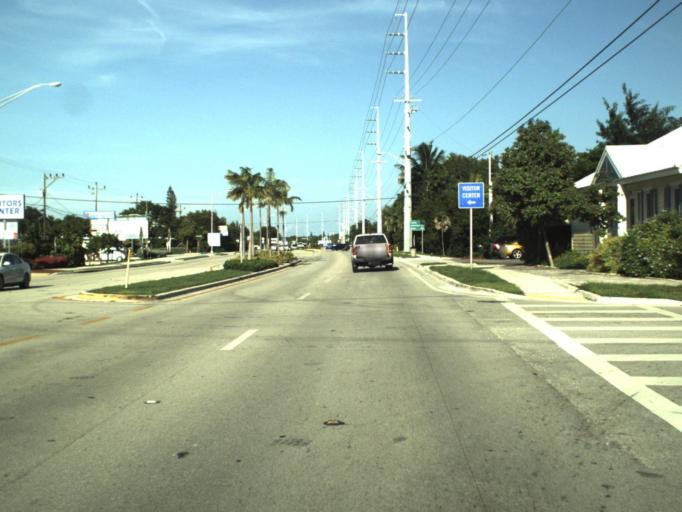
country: US
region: Florida
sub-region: Monroe County
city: Marathon
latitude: 24.7309
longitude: -81.0266
